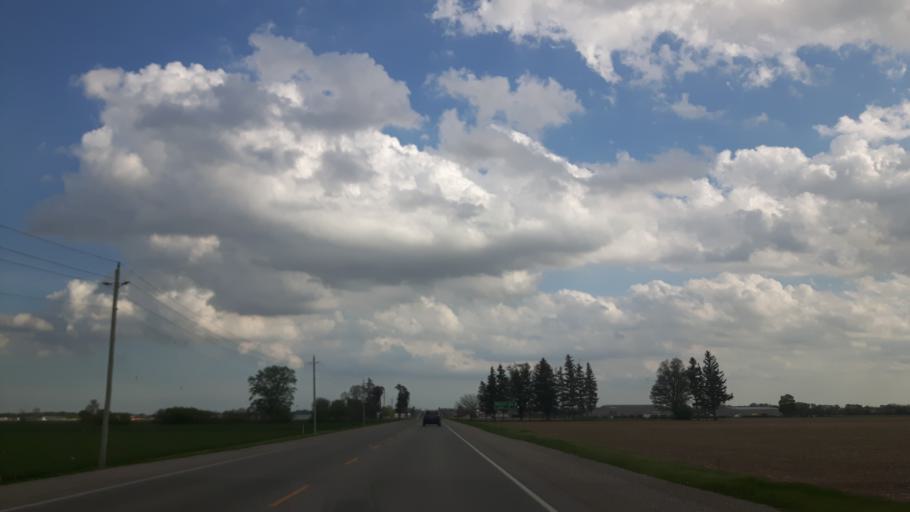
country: CA
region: Ontario
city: South Huron
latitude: 43.3739
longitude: -81.4861
